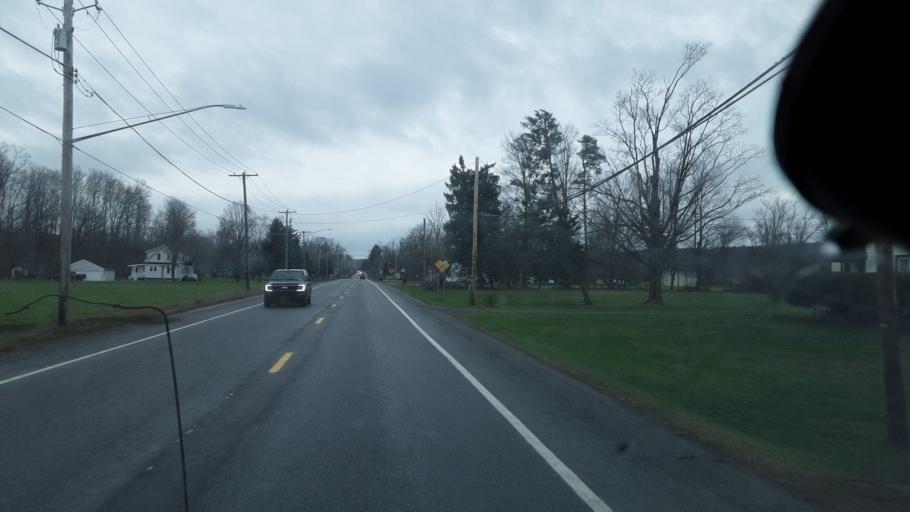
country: US
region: New York
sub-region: Erie County
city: Holland
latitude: 42.6640
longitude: -78.5565
